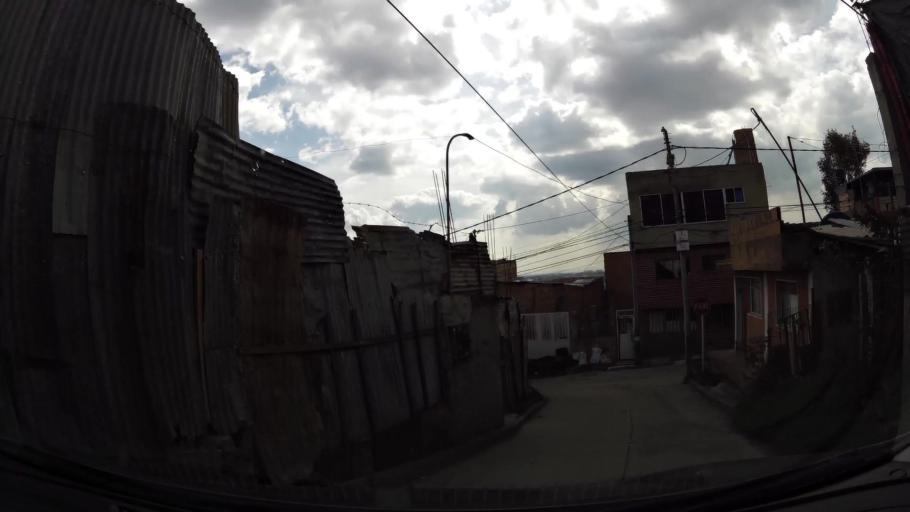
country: CO
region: Cundinamarca
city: Cota
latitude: 4.7254
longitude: -74.0847
